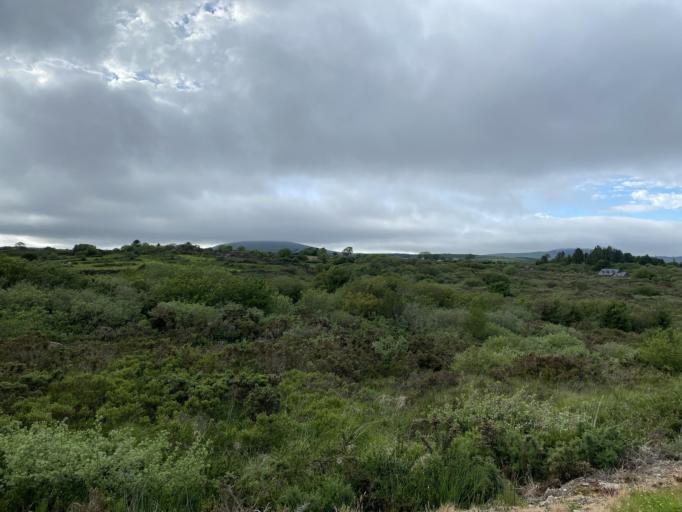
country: IE
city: Farranacoush
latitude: 51.5649
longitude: -9.4853
